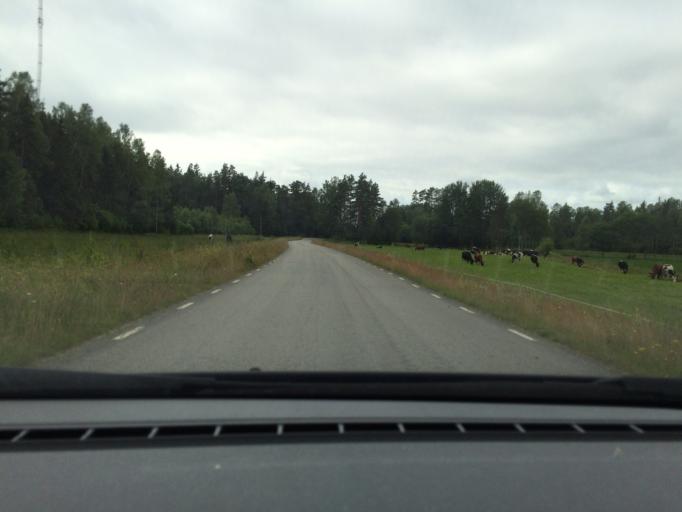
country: SE
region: Joenkoeping
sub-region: Varnamo Kommun
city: Forsheda
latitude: 57.0719
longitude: 13.8018
